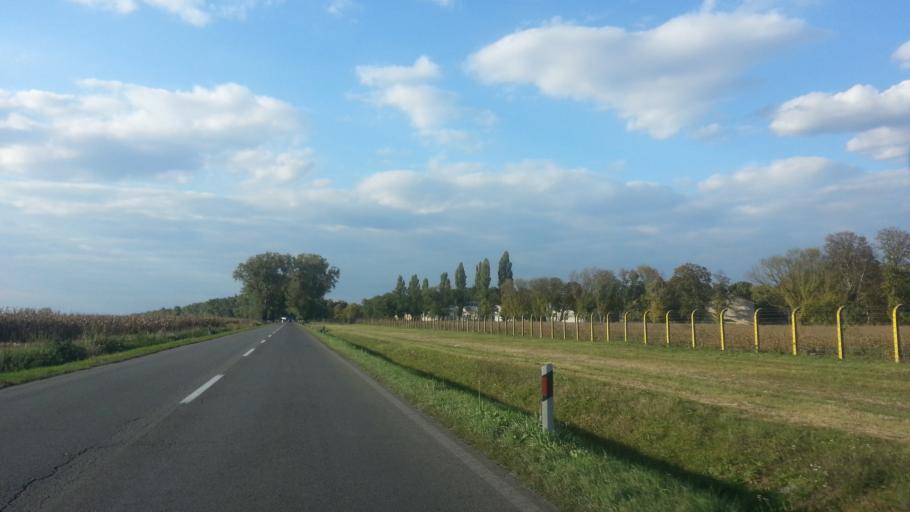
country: RS
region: Autonomna Pokrajina Vojvodina
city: Nova Pazova
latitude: 44.9213
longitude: 20.2505
